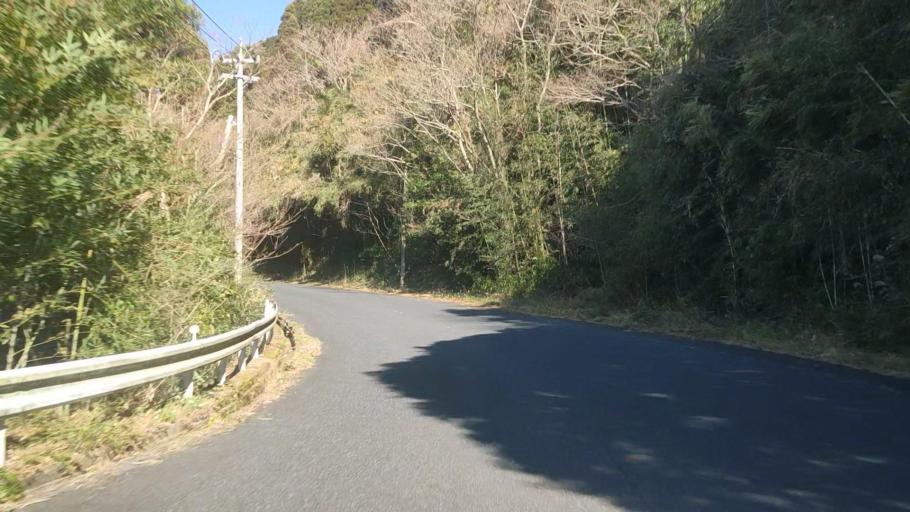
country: JP
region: Kagoshima
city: Kokubu-matsuki
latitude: 31.6699
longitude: 130.8310
